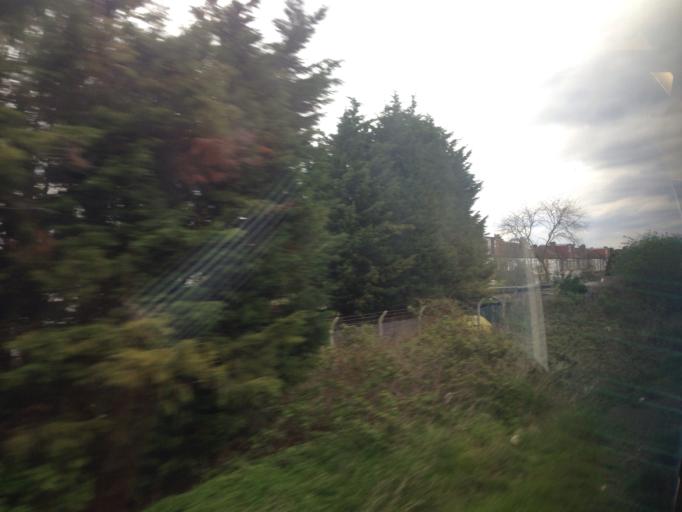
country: GB
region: England
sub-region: Greater London
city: Mitcham
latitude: 51.4103
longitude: -0.1524
